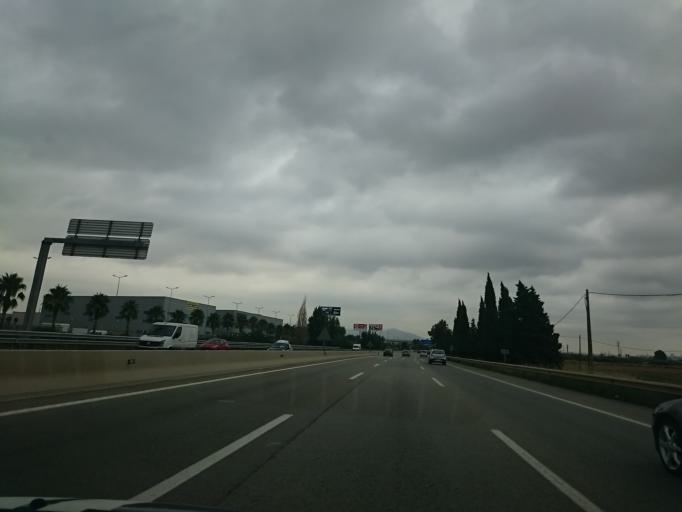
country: ES
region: Catalonia
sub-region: Provincia de Barcelona
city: Viladecans
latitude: 41.3151
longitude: 2.0342
